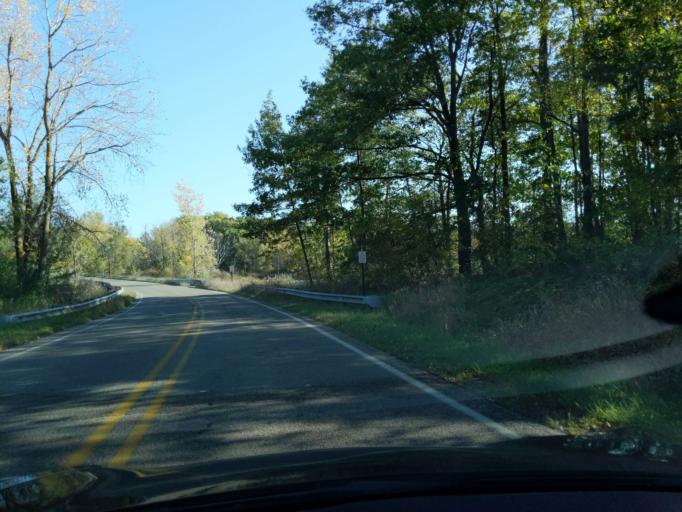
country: US
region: Michigan
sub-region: Shiawassee County
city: Laingsburg
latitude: 42.9263
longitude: -84.4185
